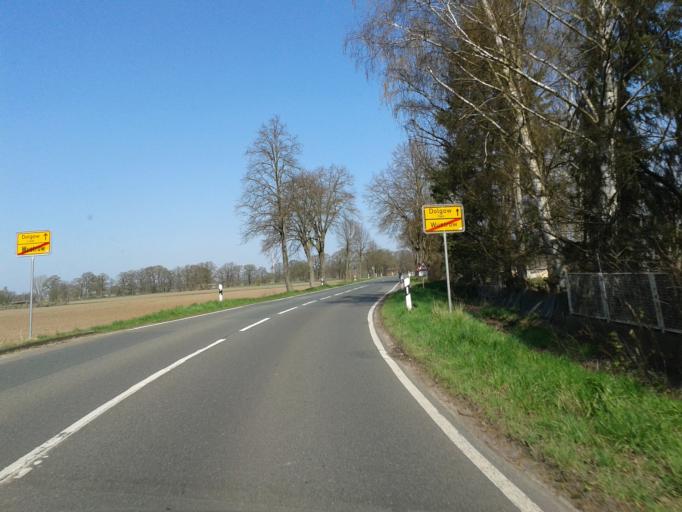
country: DE
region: Lower Saxony
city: Wustrow
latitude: 52.9275
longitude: 11.1118
